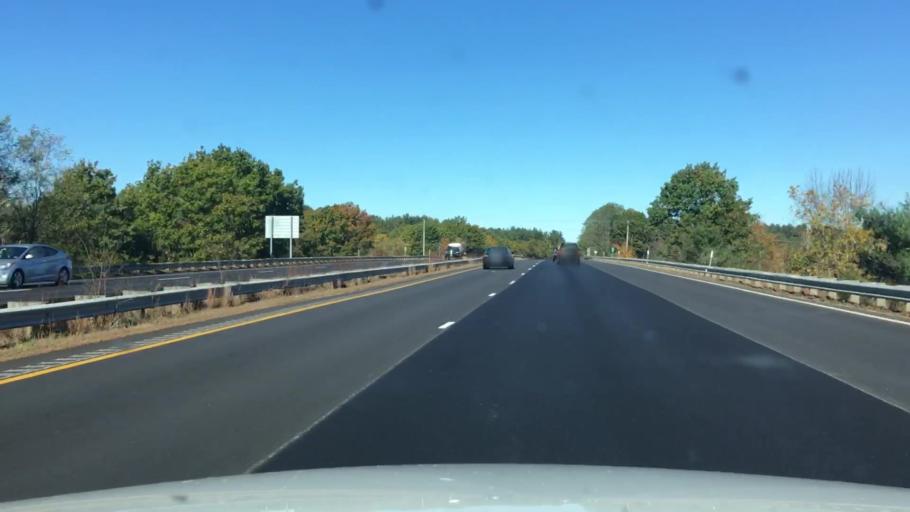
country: US
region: New Hampshire
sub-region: Strafford County
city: Dover
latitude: 43.1891
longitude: -70.8903
